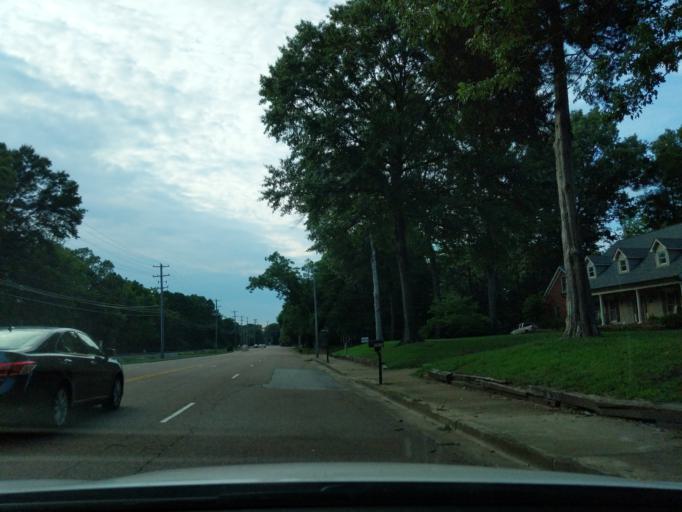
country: US
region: Tennessee
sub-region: Shelby County
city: Germantown
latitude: 35.0779
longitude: -89.7987
